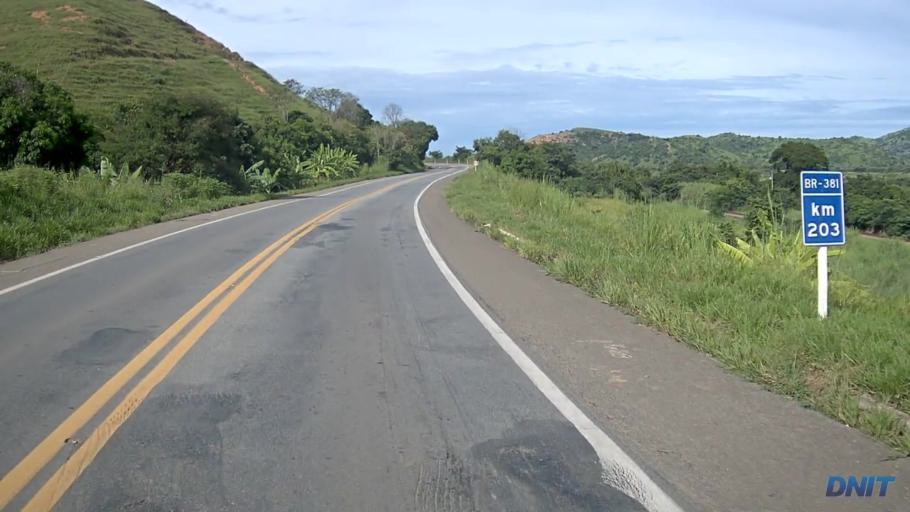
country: BR
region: Minas Gerais
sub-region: Belo Oriente
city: Belo Oriente
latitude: -19.1655
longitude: -42.2445
